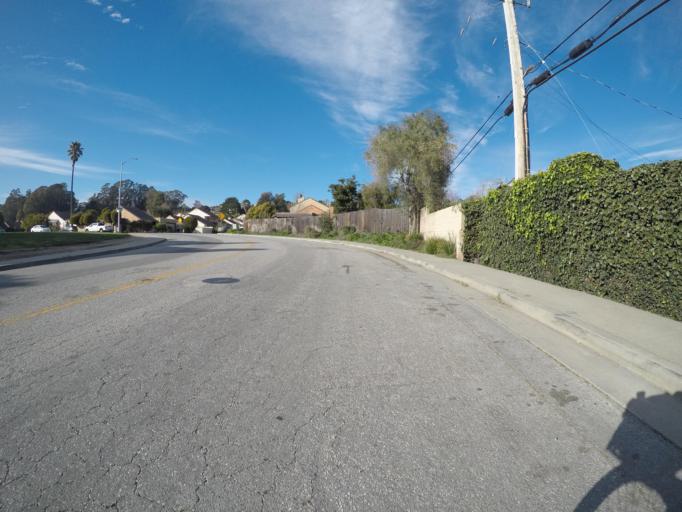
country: US
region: California
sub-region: Santa Cruz County
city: Santa Cruz
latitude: 36.9614
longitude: -122.0495
